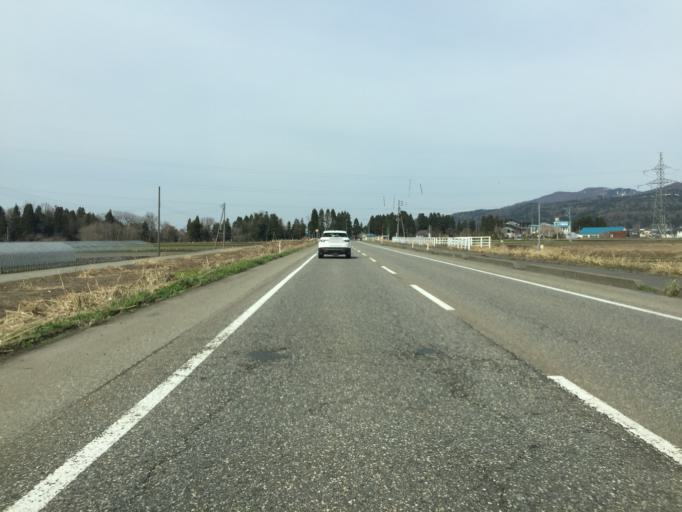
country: JP
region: Niigata
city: Ojiya
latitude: 37.3409
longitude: 138.8147
